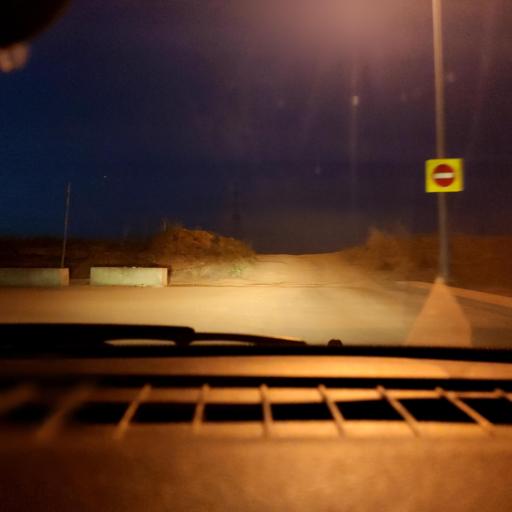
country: RU
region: Samara
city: Petra-Dubrava
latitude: 53.2911
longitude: 50.3342
